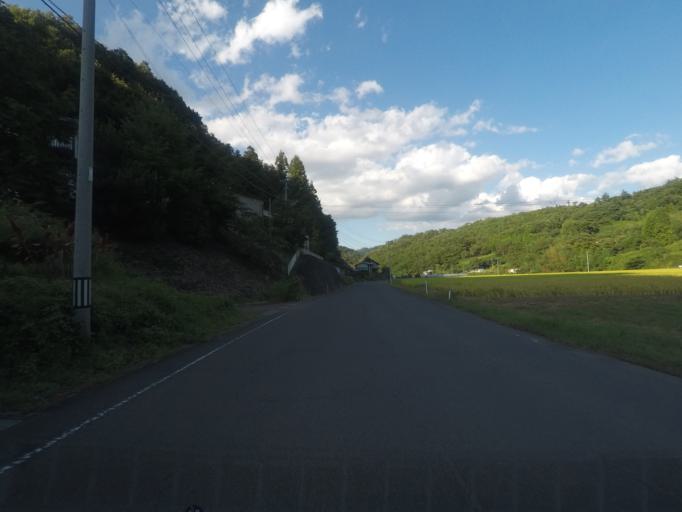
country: JP
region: Fukushima
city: Hobaramachi
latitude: 37.7520
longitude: 140.5590
